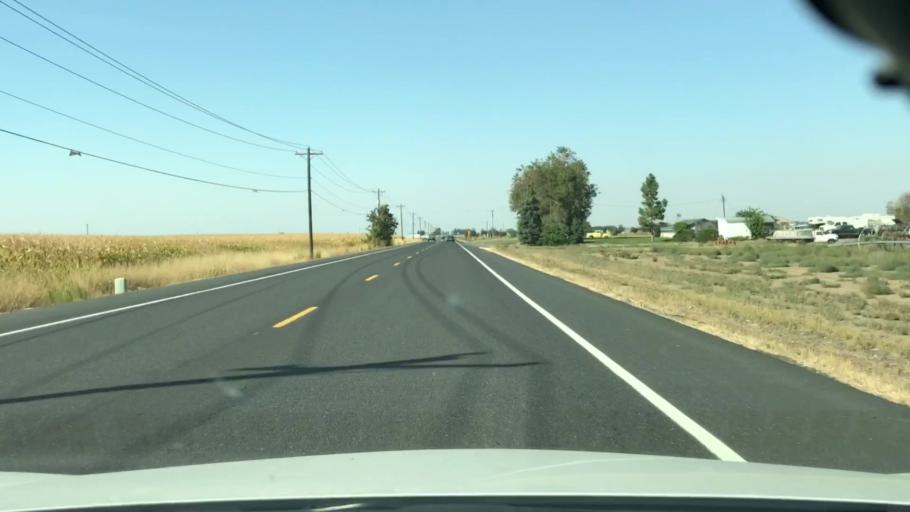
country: US
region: Washington
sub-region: Grant County
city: Moses Lake
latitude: 47.1203
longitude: -119.2358
